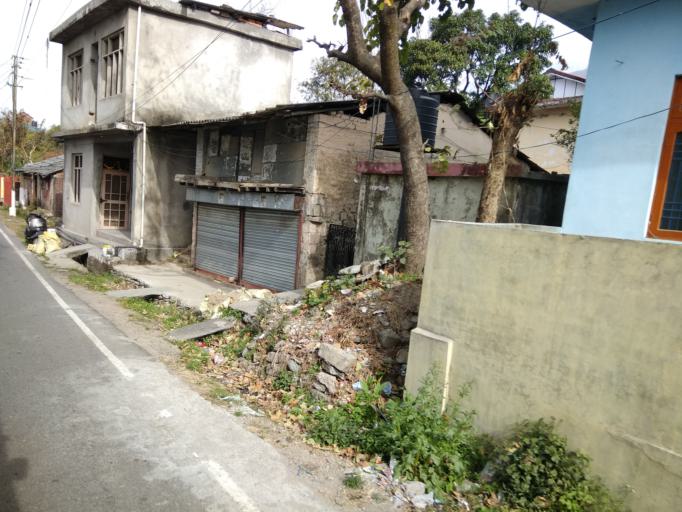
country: IN
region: Himachal Pradesh
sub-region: Kangra
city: Dharmsala
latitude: 32.1669
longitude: 76.3928
